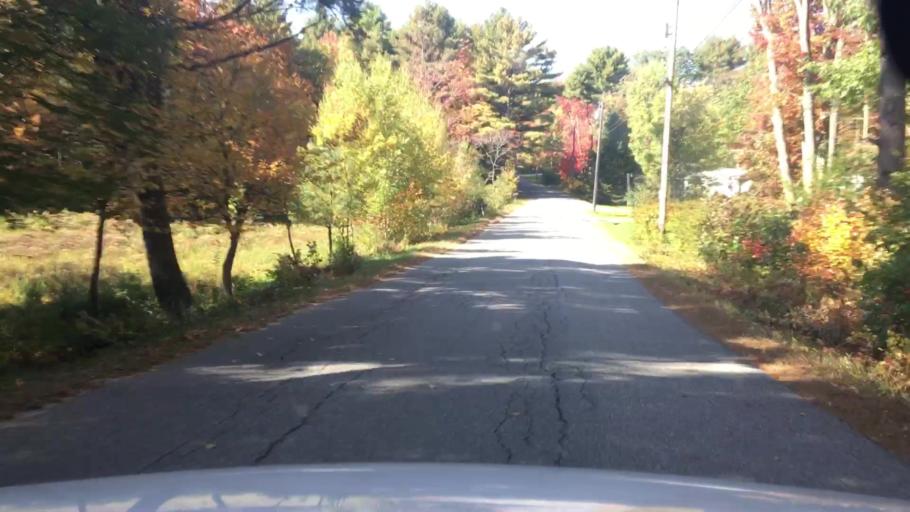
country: US
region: Maine
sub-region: Androscoggin County
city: Lisbon Falls
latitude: 44.0168
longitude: -69.9814
